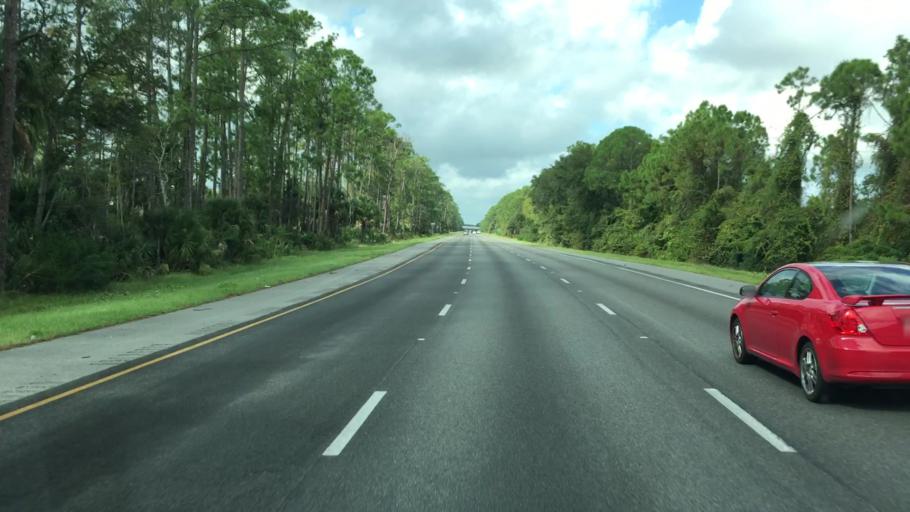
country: US
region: Florida
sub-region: Volusia County
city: Port Orange
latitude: 29.1144
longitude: -81.0343
